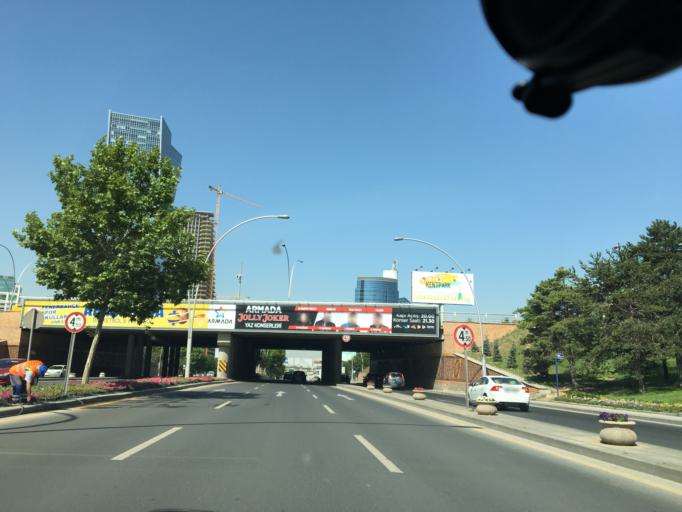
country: TR
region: Ankara
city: Ankara
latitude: 39.9130
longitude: 32.8155
